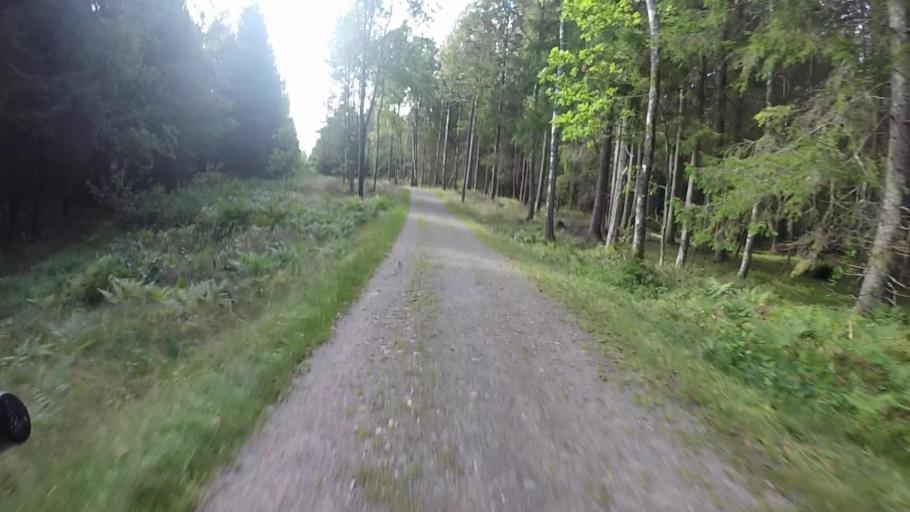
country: SE
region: Vaestra Goetaland
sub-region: Trollhattan
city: Trollhattan
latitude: 58.2531
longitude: 12.2580
